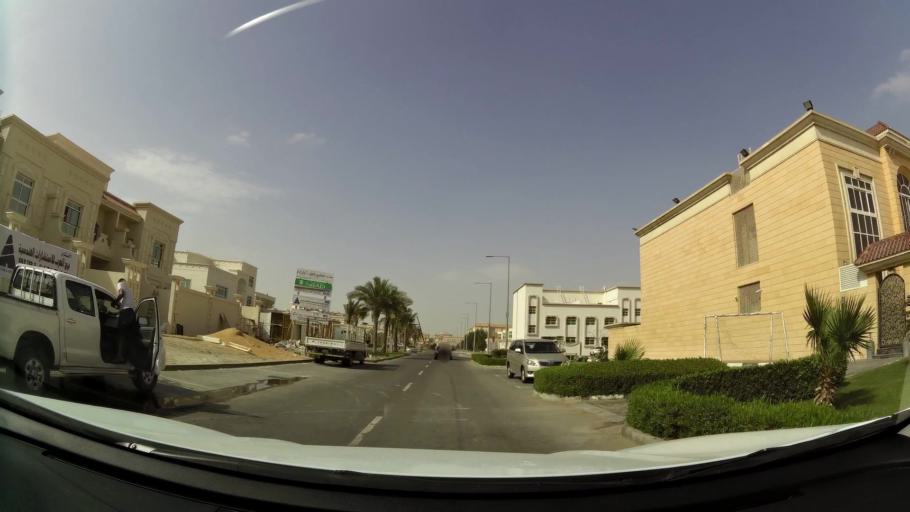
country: AE
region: Abu Dhabi
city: Abu Dhabi
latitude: 24.4230
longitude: 54.5571
